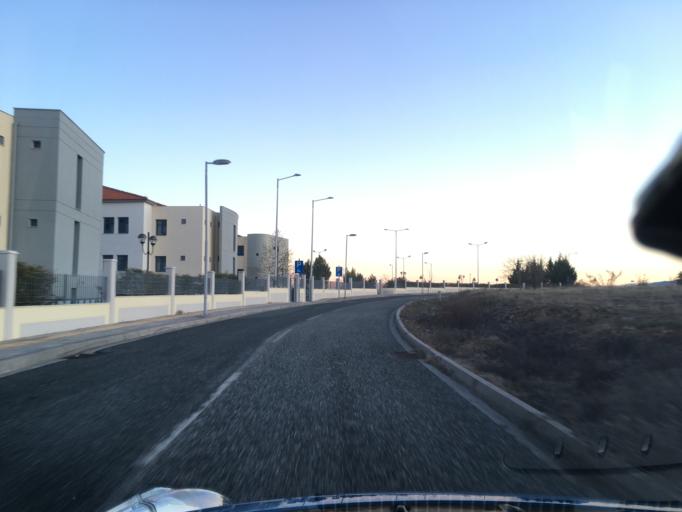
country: GR
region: West Macedonia
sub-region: Nomos Kozanis
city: Kozani
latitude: 40.2722
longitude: 21.7561
